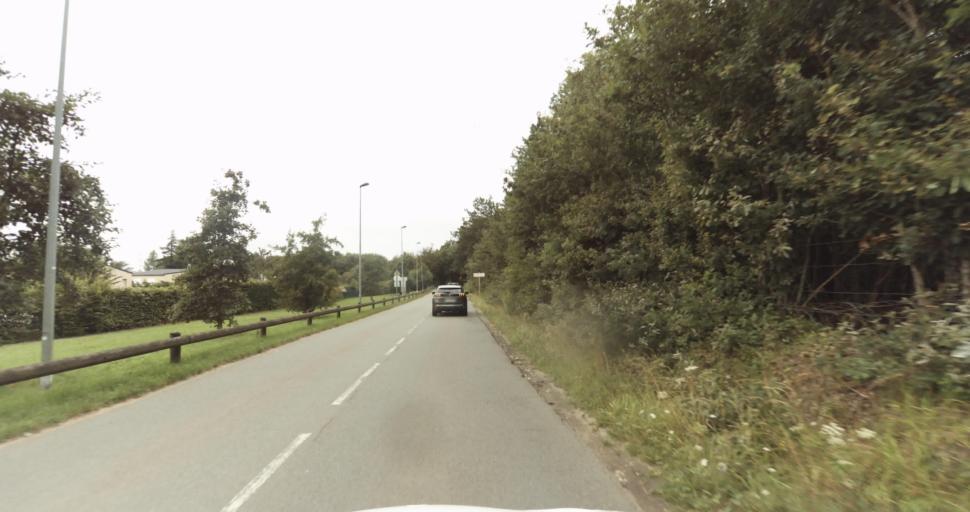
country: FR
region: Haute-Normandie
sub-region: Departement de l'Eure
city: Gravigny
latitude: 49.0361
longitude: 1.1743
